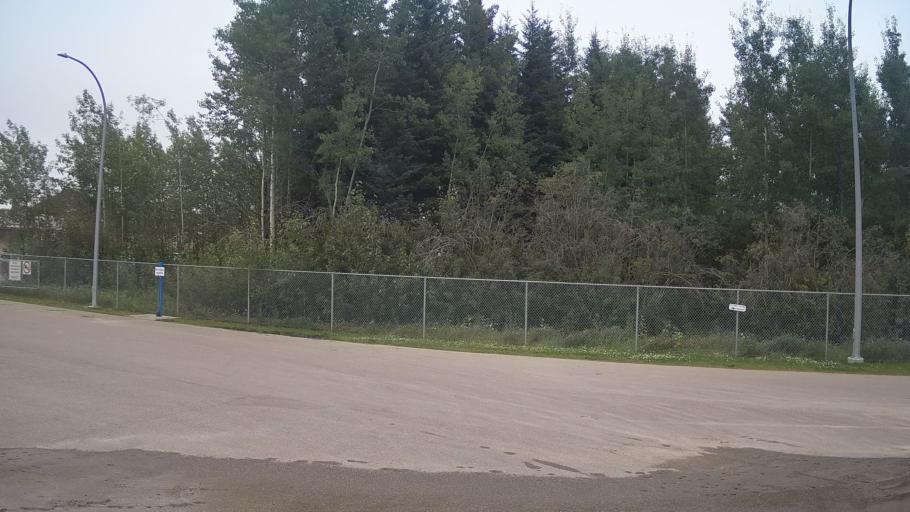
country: CA
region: Alberta
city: Edson
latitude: 53.5763
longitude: -116.4430
